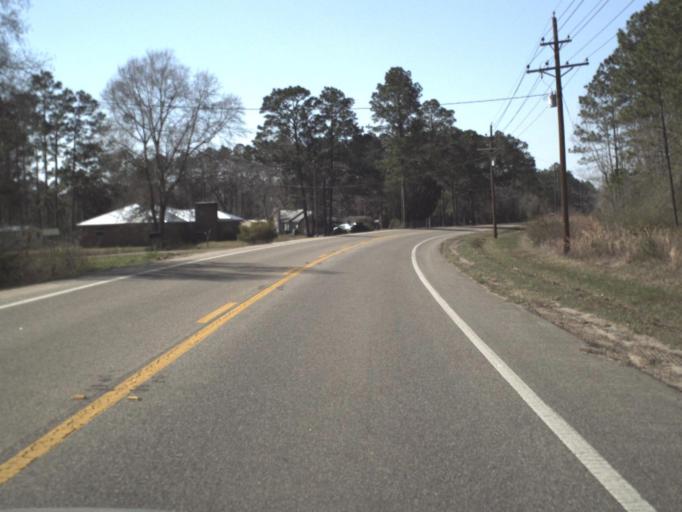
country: US
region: Florida
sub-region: Calhoun County
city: Blountstown
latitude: 30.4714
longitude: -85.0900
